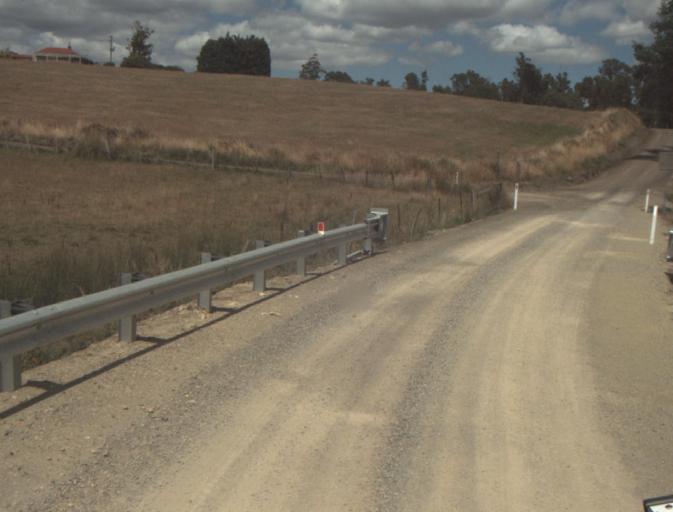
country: AU
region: Tasmania
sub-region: Launceston
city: Mayfield
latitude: -41.2119
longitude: 147.1429
